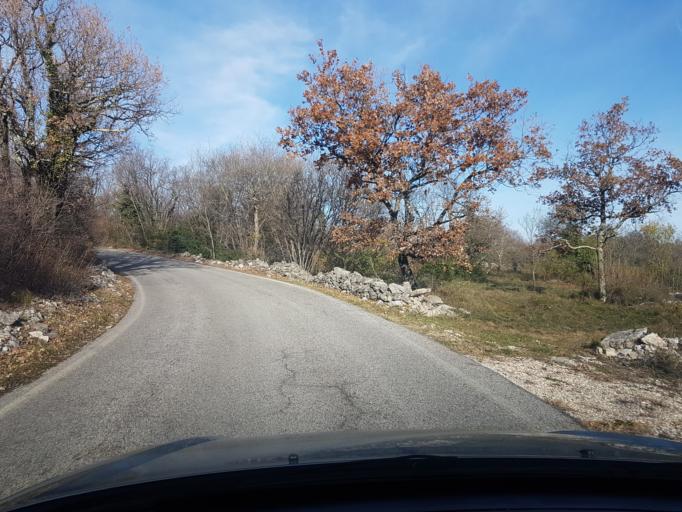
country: IT
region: Friuli Venezia Giulia
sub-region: Provincia di Trieste
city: Sistiana-Visogliano
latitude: 45.7813
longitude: 13.6406
